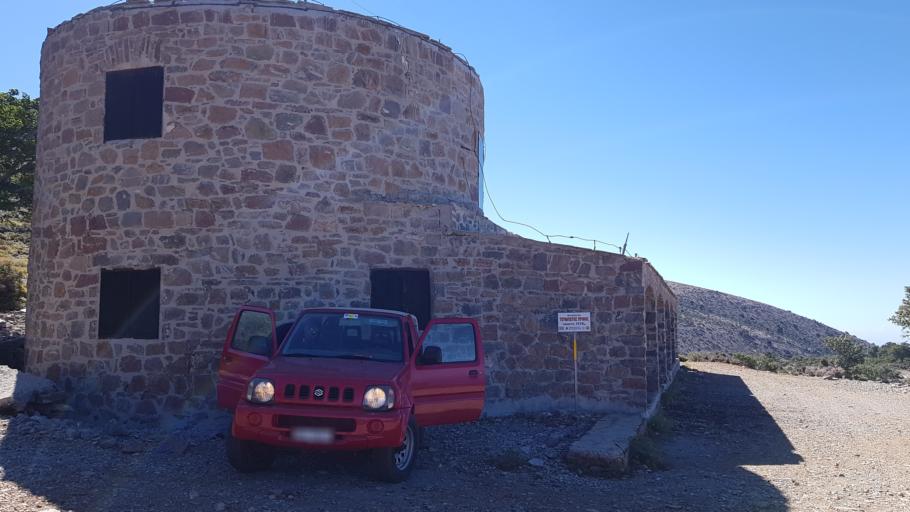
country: GR
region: Crete
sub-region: Nomos Rethymnis
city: Zoniana
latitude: 35.2071
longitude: 24.7618
